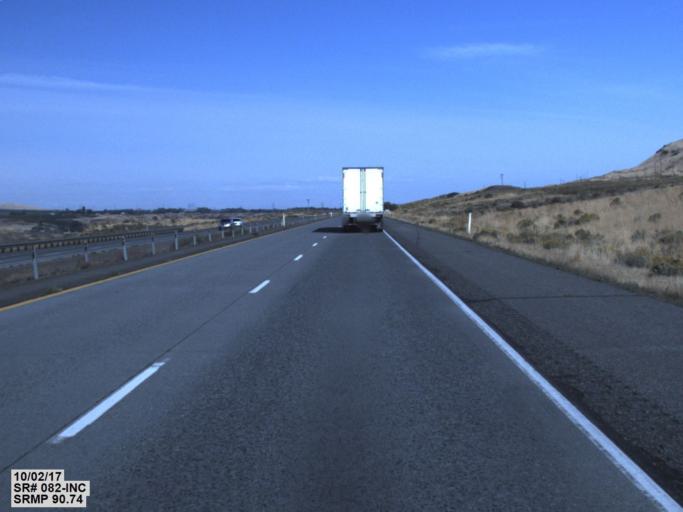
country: US
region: Washington
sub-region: Benton County
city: Benton City
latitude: 46.2580
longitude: -119.5912
